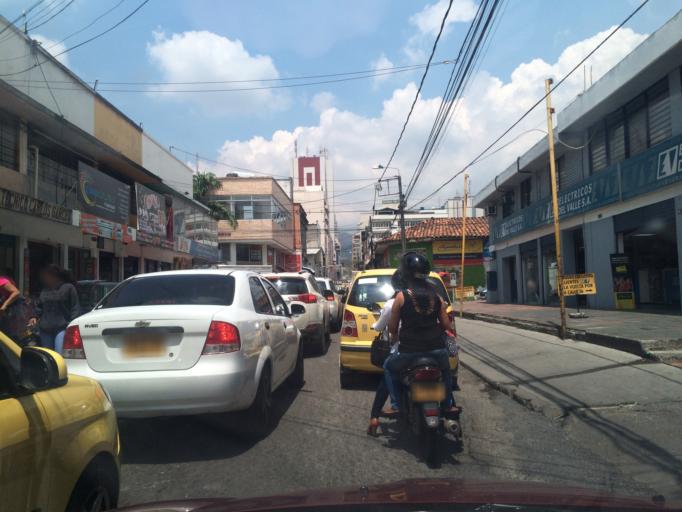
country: CO
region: Valle del Cauca
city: Cali
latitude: 3.4542
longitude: -76.5287
